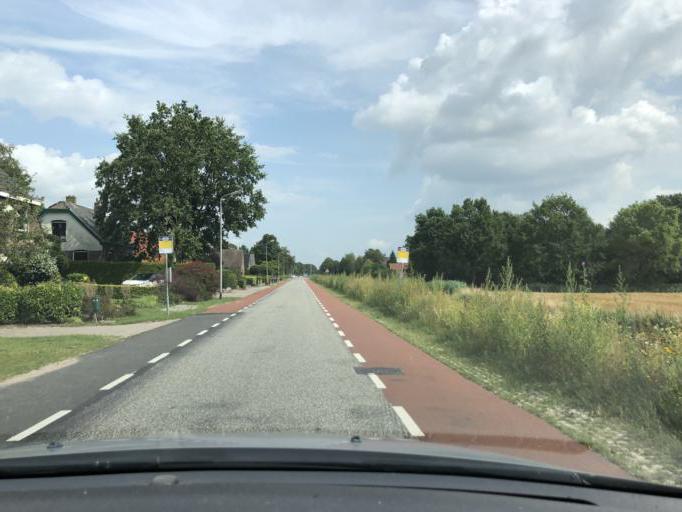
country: NL
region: Drenthe
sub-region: Gemeente Hoogeveen
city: Hoogeveen
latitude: 52.7617
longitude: 6.6041
